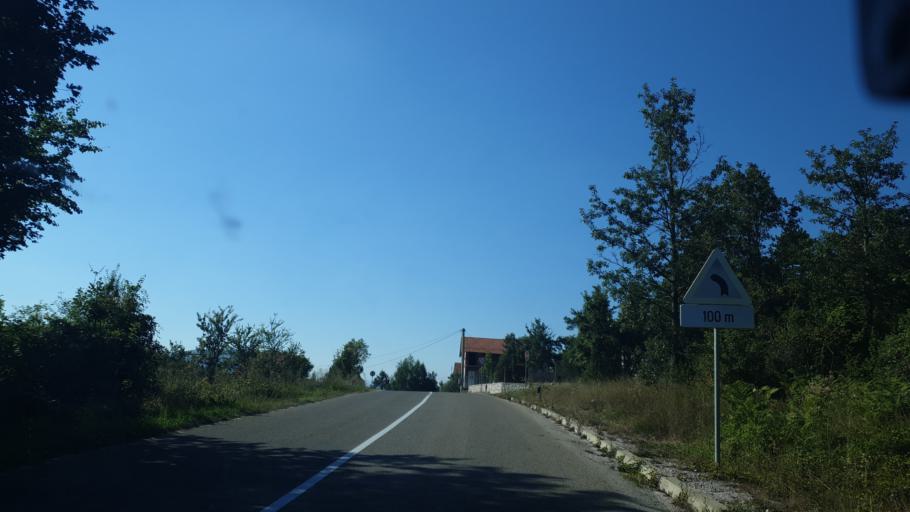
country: RS
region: Central Serbia
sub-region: Zlatiborski Okrug
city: Cajetina
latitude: 43.7255
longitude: 19.8084
